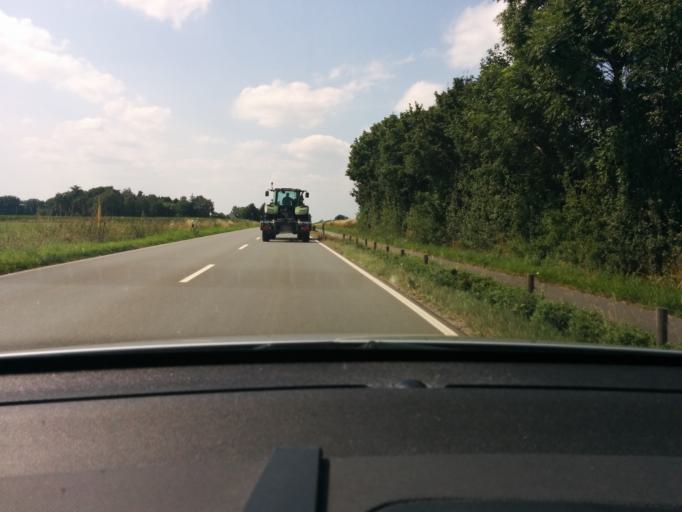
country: DE
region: North Rhine-Westphalia
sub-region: Regierungsbezirk Munster
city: Steinfurt
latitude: 52.1638
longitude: 7.3047
